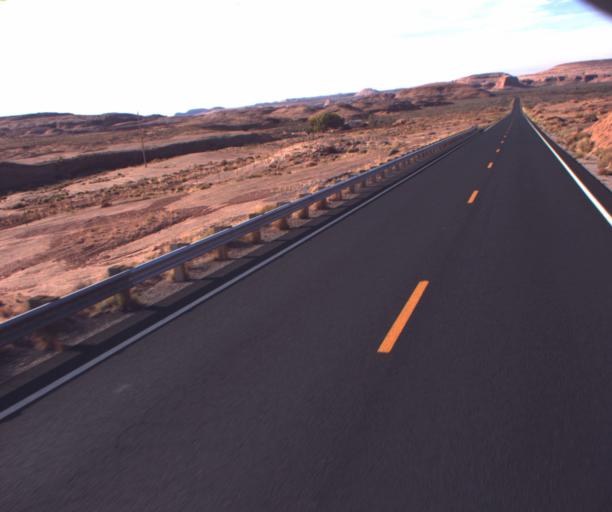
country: US
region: Arizona
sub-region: Apache County
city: Many Farms
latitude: 36.7842
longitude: -109.6557
